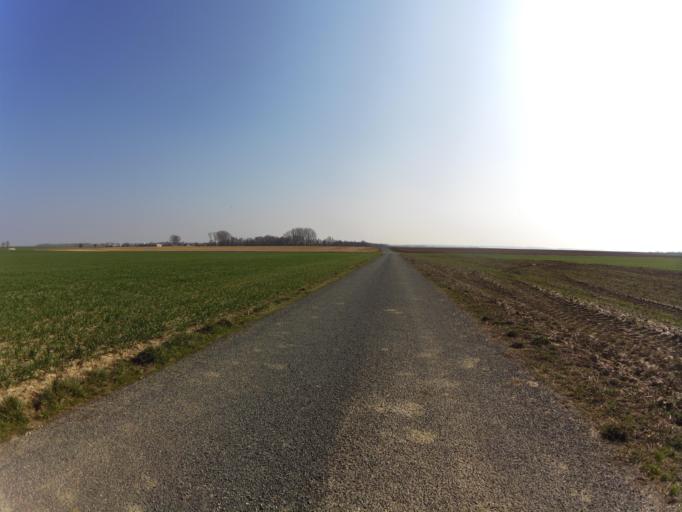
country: DE
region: Bavaria
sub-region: Regierungsbezirk Unterfranken
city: Sulzdorf
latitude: 49.6671
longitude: 9.9160
